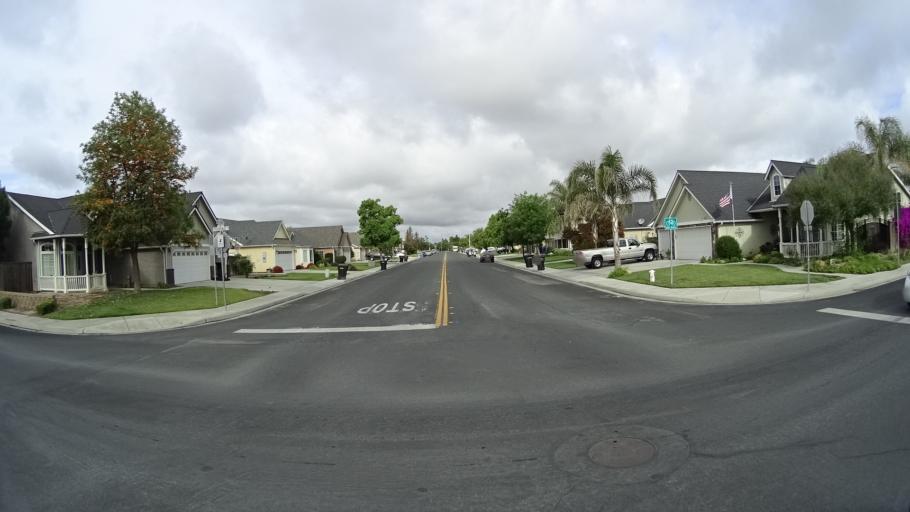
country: US
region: California
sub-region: Kings County
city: Lucerne
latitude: 36.3511
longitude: -119.6684
